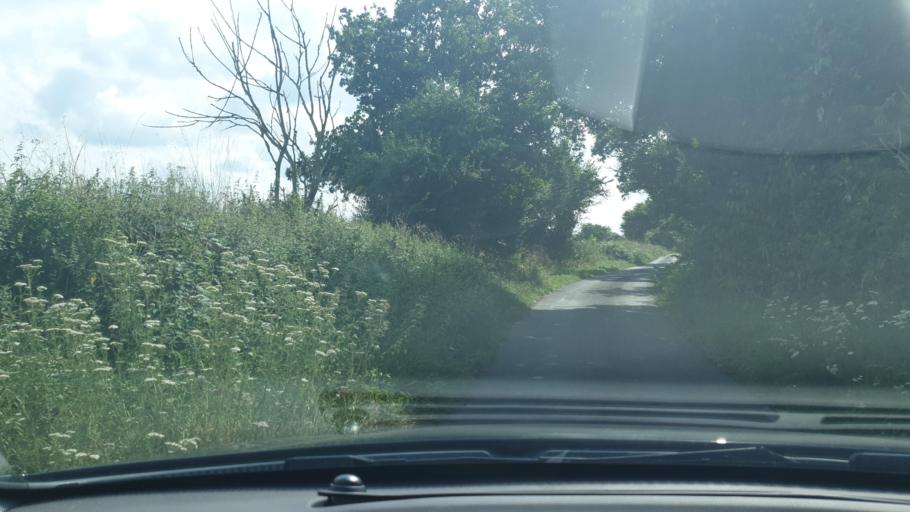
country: GB
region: England
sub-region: Essex
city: Manningtree
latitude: 51.9253
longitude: 1.0286
